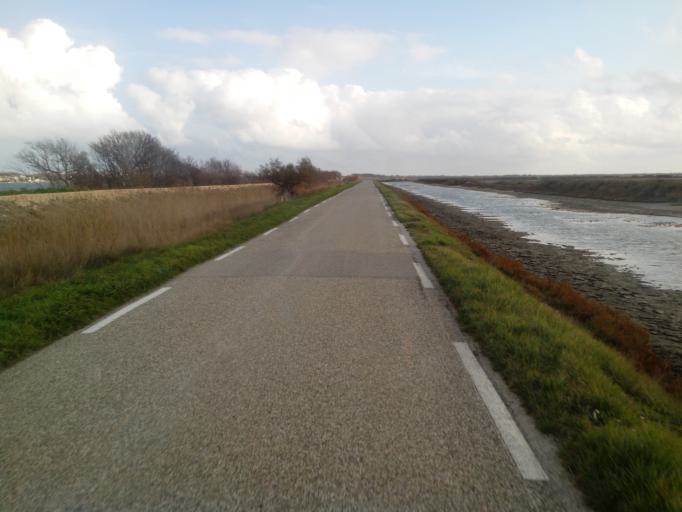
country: FR
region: Provence-Alpes-Cote d'Azur
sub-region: Departement des Bouches-du-Rhone
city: Port-Saint-Louis-du-Rhone
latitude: 43.3884
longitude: 4.7872
